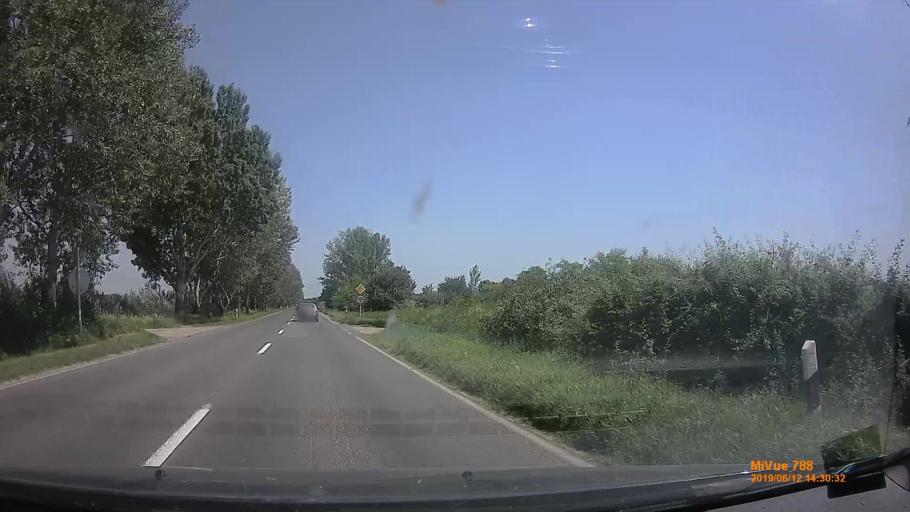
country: HU
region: Csongrad
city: Kiszombor
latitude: 46.2004
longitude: 20.3930
